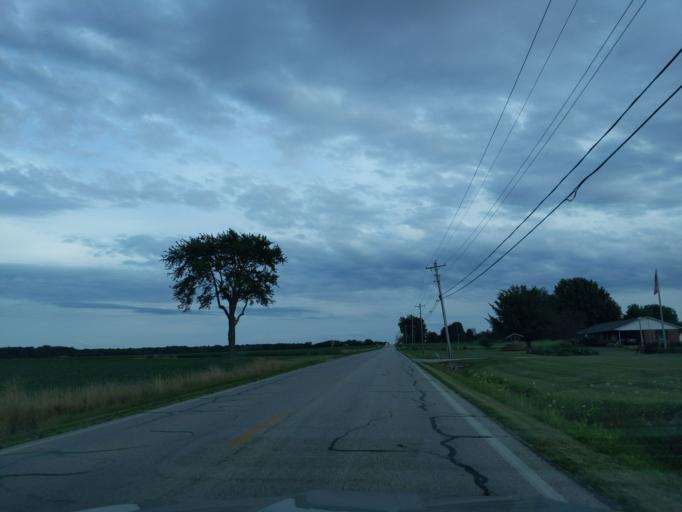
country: US
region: Indiana
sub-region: Ripley County
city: Sunman
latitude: 39.2603
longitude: -85.0945
